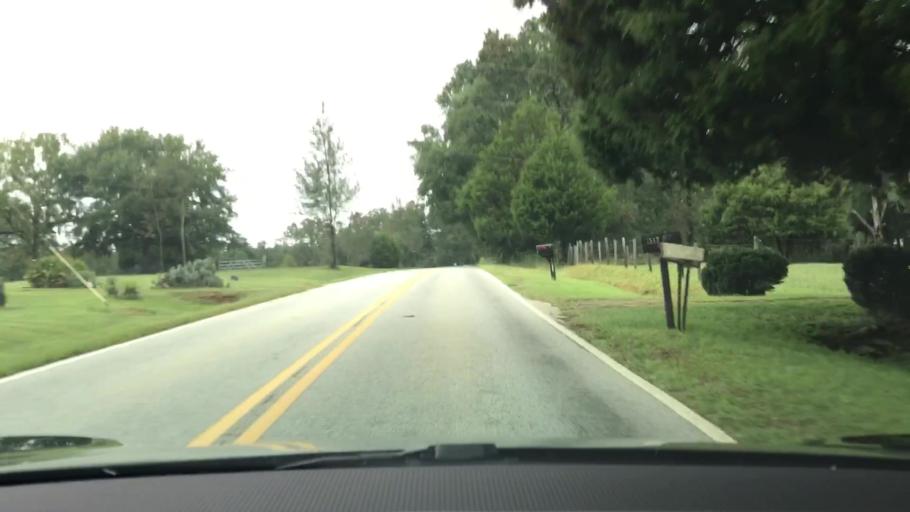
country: US
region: Georgia
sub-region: Barrow County
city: Auburn
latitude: 34.0607
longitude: -83.8342
